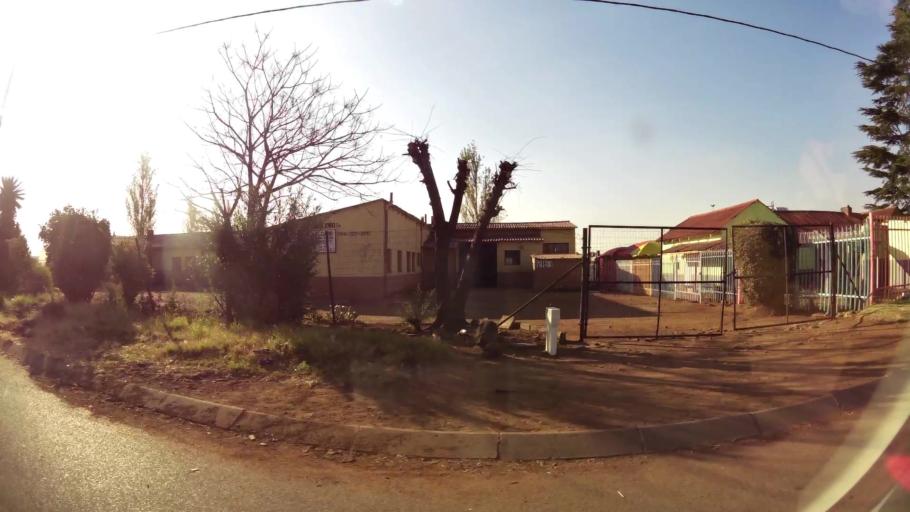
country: ZA
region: Gauteng
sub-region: City of Johannesburg Metropolitan Municipality
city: Soweto
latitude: -26.2677
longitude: 27.8714
